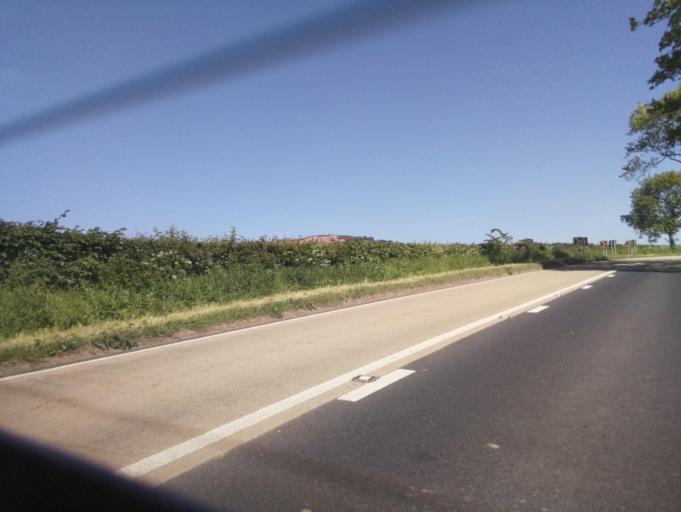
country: GB
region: Scotland
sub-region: Fife
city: Balmullo
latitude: 56.3707
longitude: -2.9315
